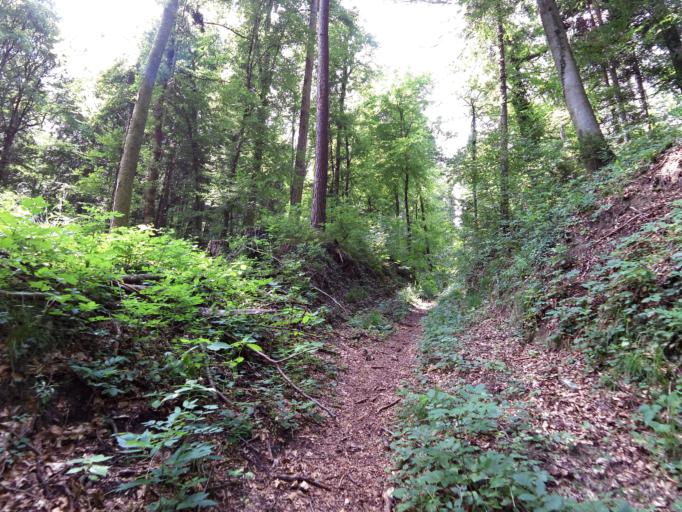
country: CH
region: Thurgau
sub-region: Kreuzlingen District
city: Ermatingen
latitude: 47.6595
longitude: 9.0745
